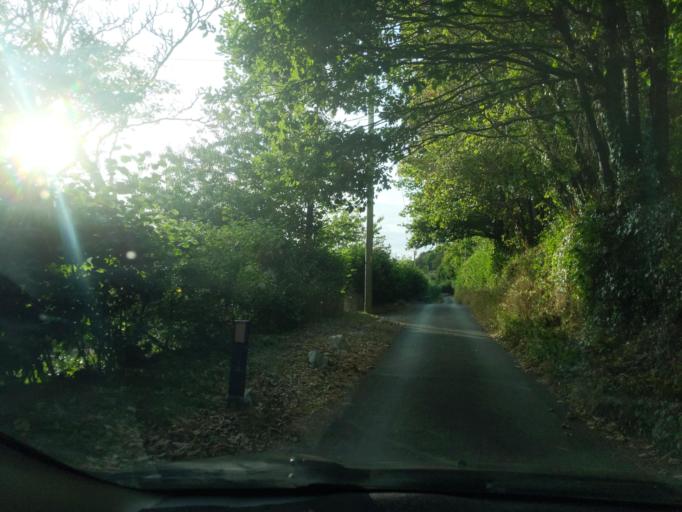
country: GB
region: England
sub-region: Devon
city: Salcombe
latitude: 50.2286
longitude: -3.7930
